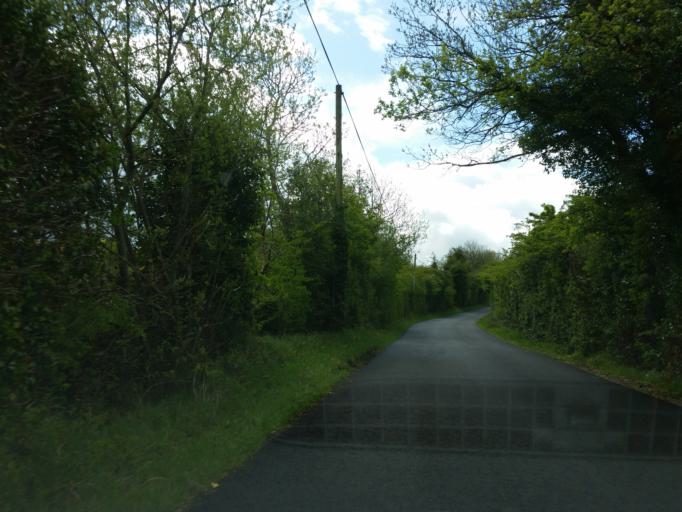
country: GB
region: Northern Ireland
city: Lisnaskea
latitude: 54.2365
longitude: -7.3670
